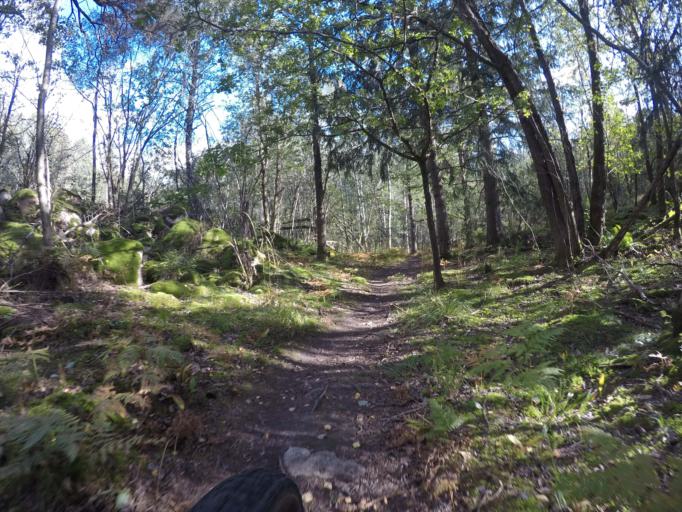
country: SE
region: Vaestmanland
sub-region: Kopings Kommun
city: Koping
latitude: 59.5075
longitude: 16.0235
